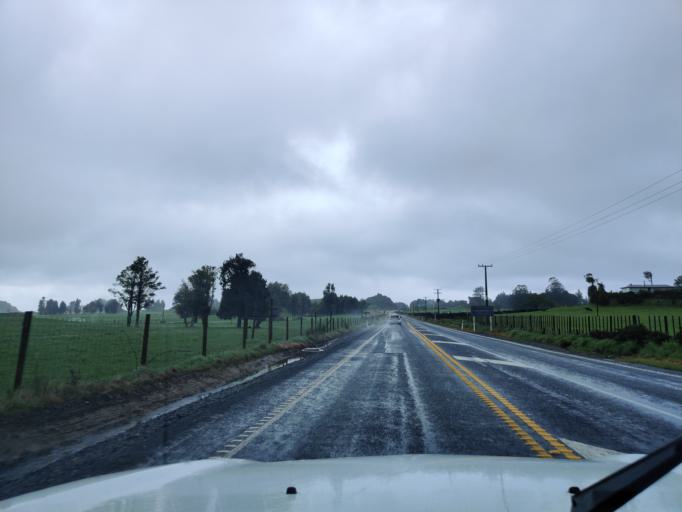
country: NZ
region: Bay of Plenty
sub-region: Rotorua District
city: Rotorua
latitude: -38.0507
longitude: 176.0776
